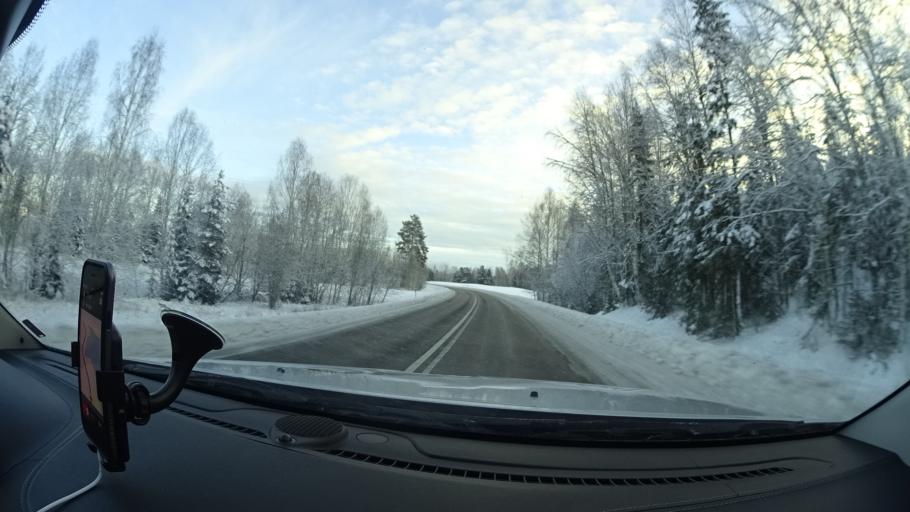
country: SE
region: Jaemtland
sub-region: Ragunda Kommun
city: Hammarstrand
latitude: 63.1538
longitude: 16.2285
